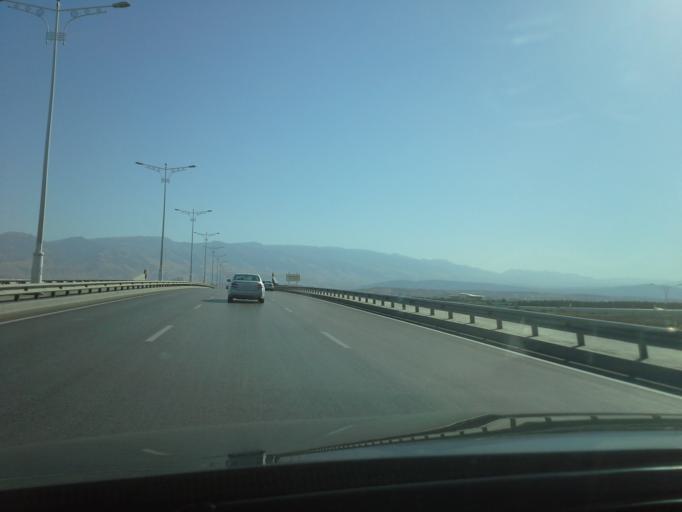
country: TM
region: Ahal
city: Ashgabat
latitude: 37.9825
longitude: 58.4014
